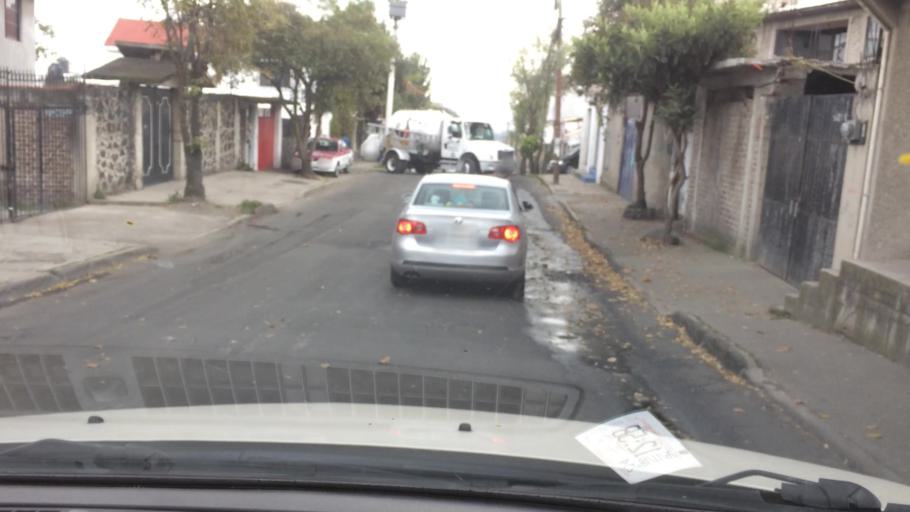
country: MX
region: Mexico City
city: Tlalpan
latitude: 19.2776
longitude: -99.2073
